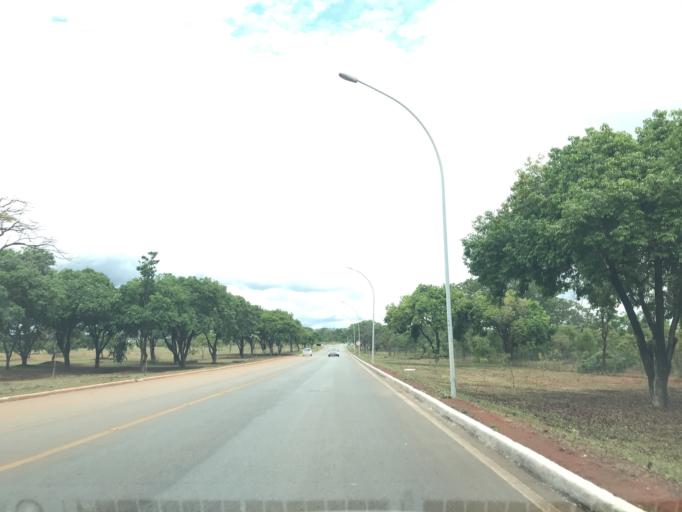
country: BR
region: Federal District
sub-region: Brasilia
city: Brasilia
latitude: -15.7959
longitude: -47.8392
